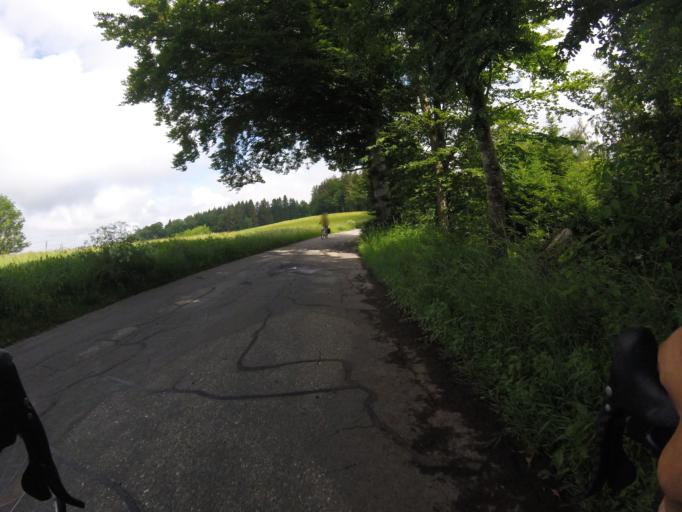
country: CH
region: Bern
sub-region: Bern-Mittelland District
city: Walkringen
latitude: 46.9601
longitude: 7.5986
